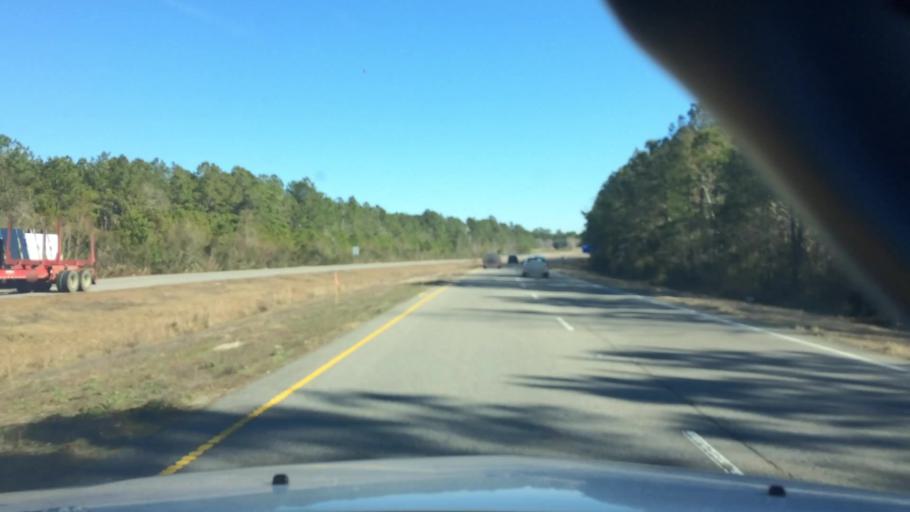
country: US
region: North Carolina
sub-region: Brunswick County
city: Shallotte
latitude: 33.9701
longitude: -78.4113
